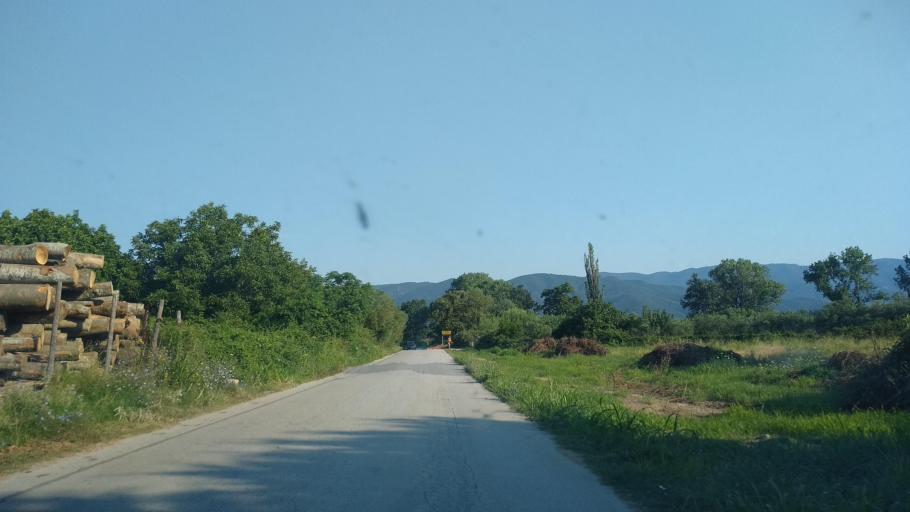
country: GR
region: Central Macedonia
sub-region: Nomos Thessalonikis
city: Stavros
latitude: 40.6742
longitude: 23.6895
